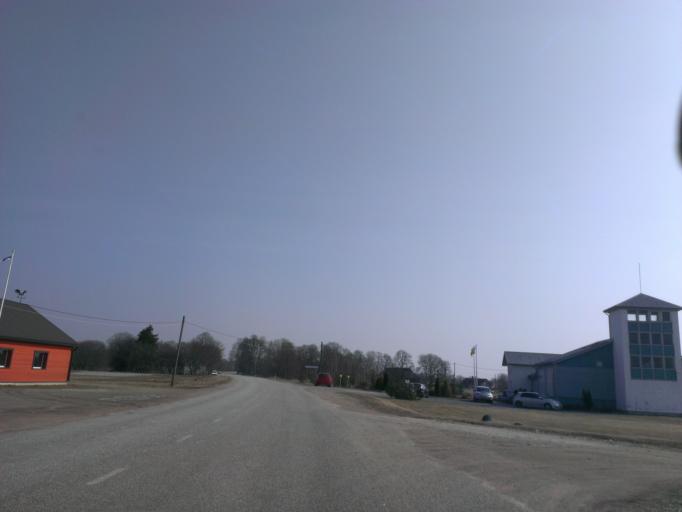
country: EE
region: Saare
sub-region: Kuressaare linn
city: Kuressaare
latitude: 58.3019
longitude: 22.7072
